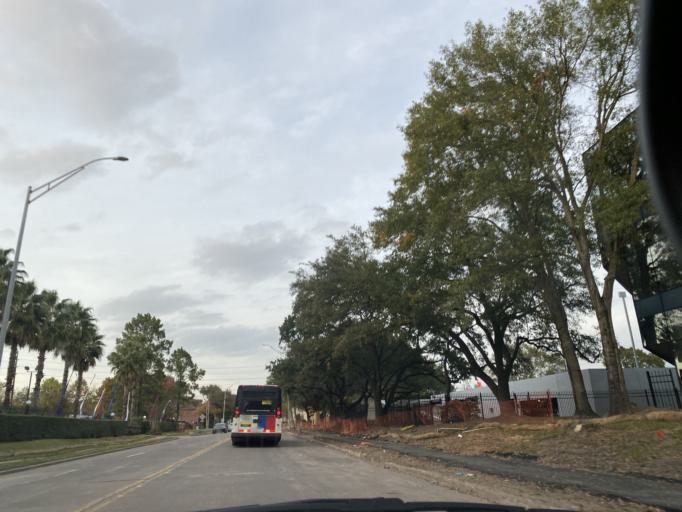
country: US
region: Texas
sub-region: Harris County
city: Bunker Hill Village
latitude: 29.7282
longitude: -95.5680
